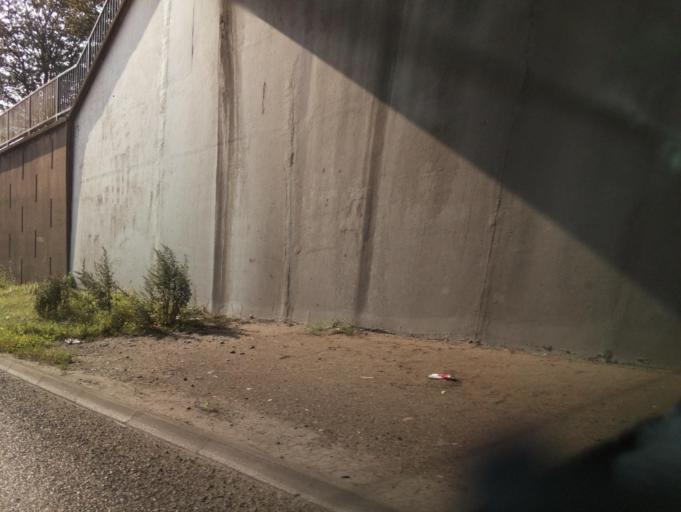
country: GB
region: England
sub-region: Sandwell
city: West Bromwich
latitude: 52.5200
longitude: -1.9870
